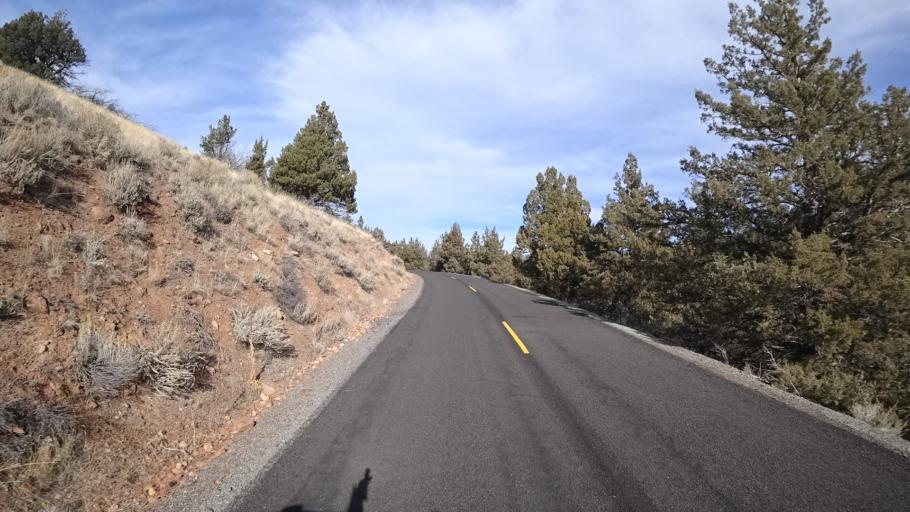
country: US
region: California
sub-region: Siskiyou County
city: Weed
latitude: 41.4999
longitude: -122.3899
